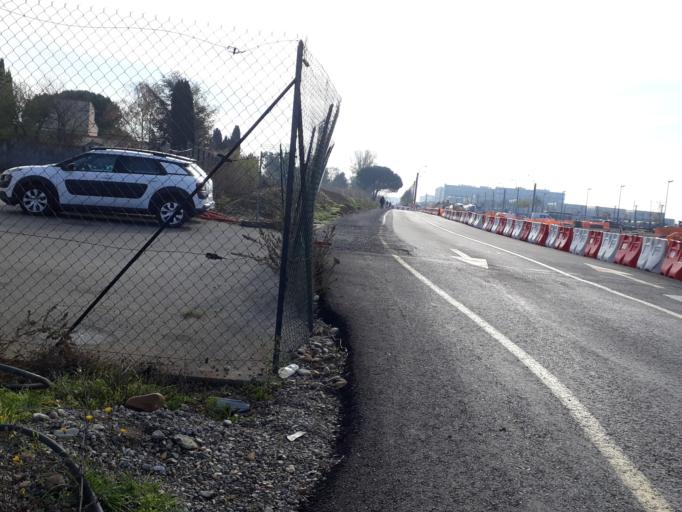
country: FR
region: Midi-Pyrenees
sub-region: Departement de la Haute-Garonne
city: Beauzelle
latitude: 43.6655
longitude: 1.3617
